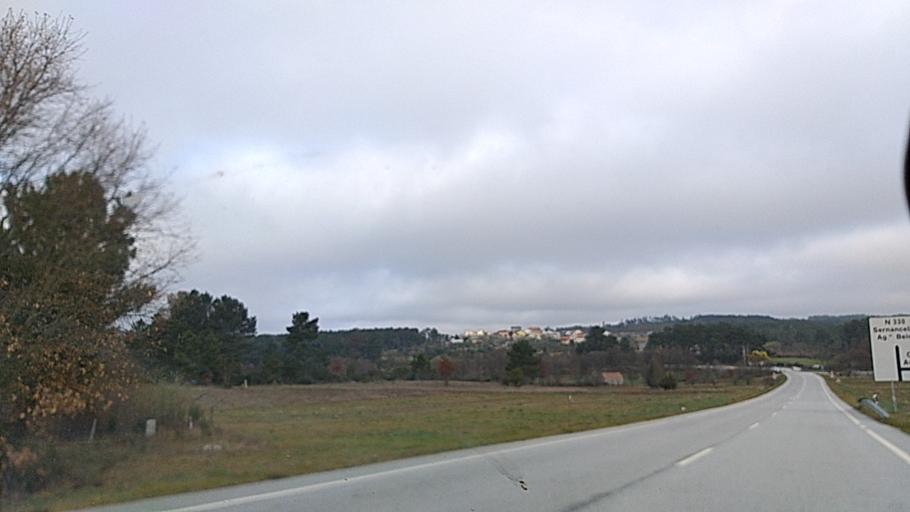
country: PT
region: Guarda
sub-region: Fornos de Algodres
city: Fornos de Algodres
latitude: 40.7155
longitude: -7.4872
